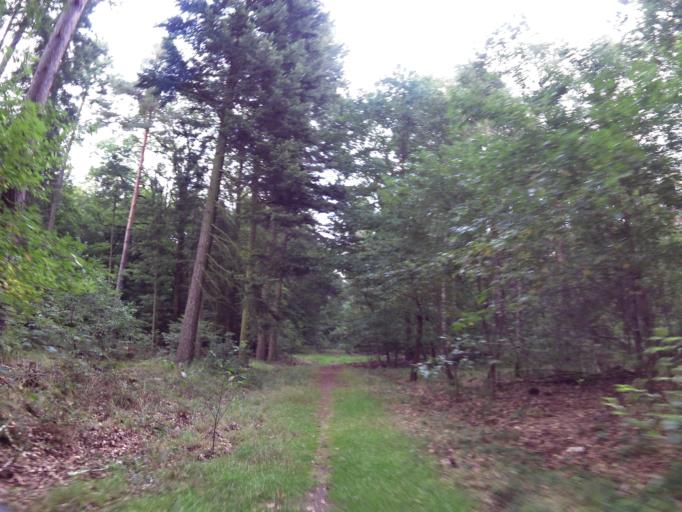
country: DE
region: Hesse
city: Morfelden-Walldorf
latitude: 50.0175
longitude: 8.5979
